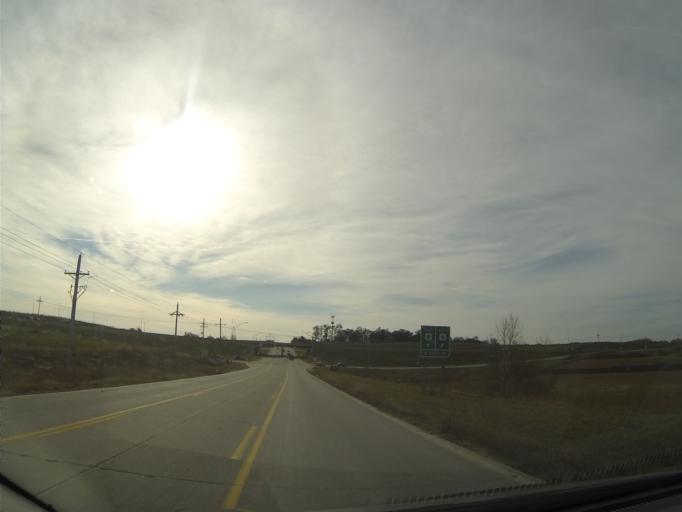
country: US
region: Nebraska
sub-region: Douglas County
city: Elkhorn
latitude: 41.2651
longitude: -96.2157
